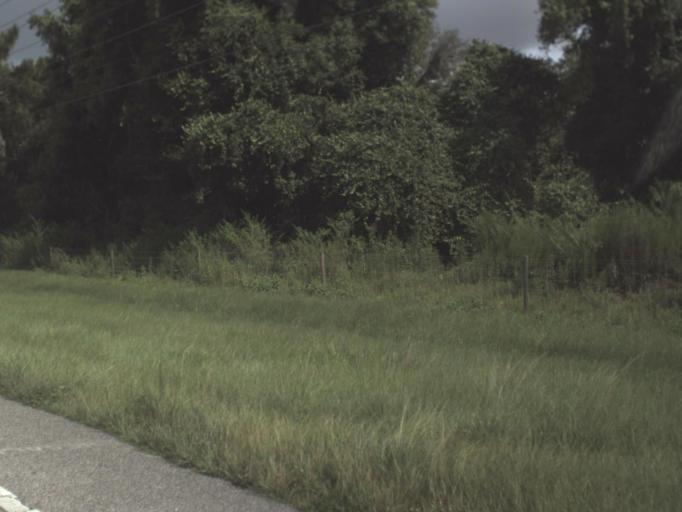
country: US
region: Florida
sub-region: Pasco County
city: Land O' Lakes
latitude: 28.3221
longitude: -82.4563
